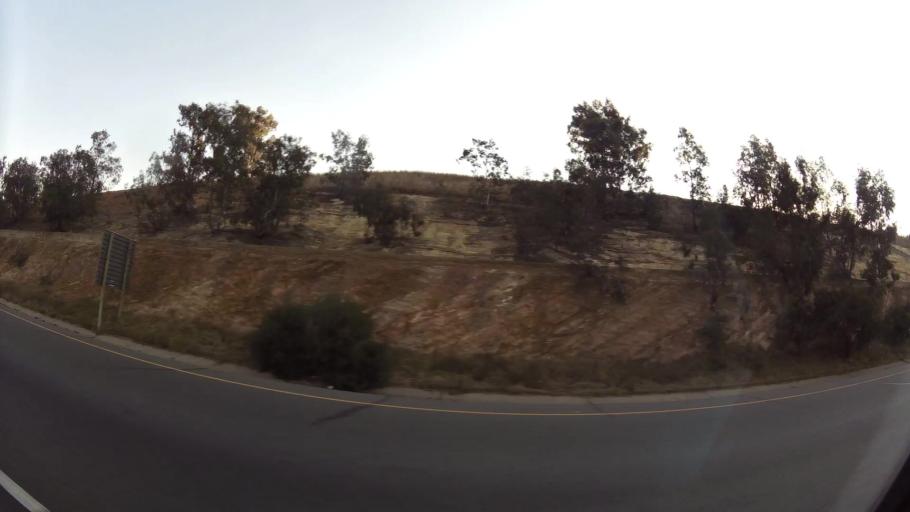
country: ZA
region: Gauteng
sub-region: City of Johannesburg Metropolitan Municipality
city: Johannesburg
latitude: -26.2091
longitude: 27.9569
